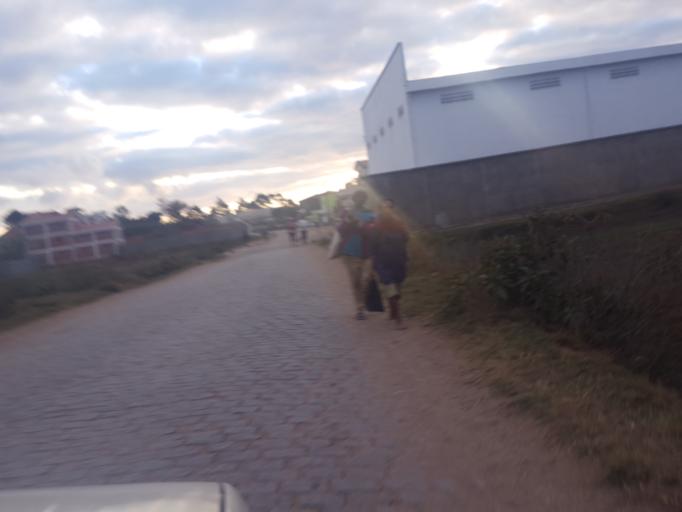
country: MG
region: Analamanga
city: Antananarivo
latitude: -18.9795
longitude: 47.5425
